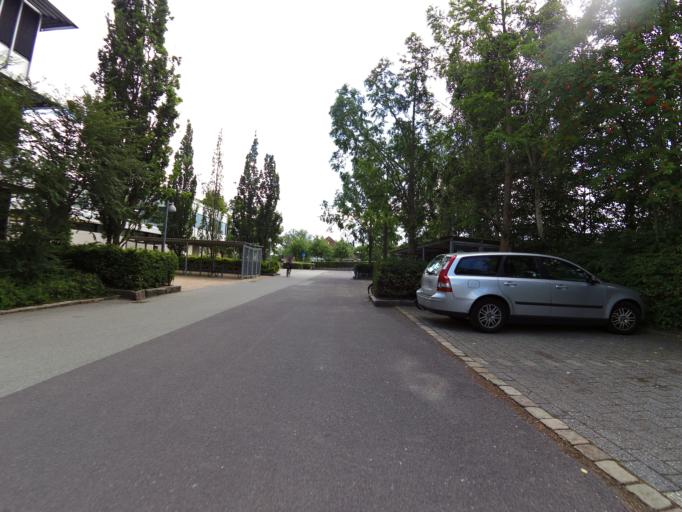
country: DK
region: Capital Region
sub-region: Frederiksberg Kommune
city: Frederiksberg
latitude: 55.7207
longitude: 12.5415
